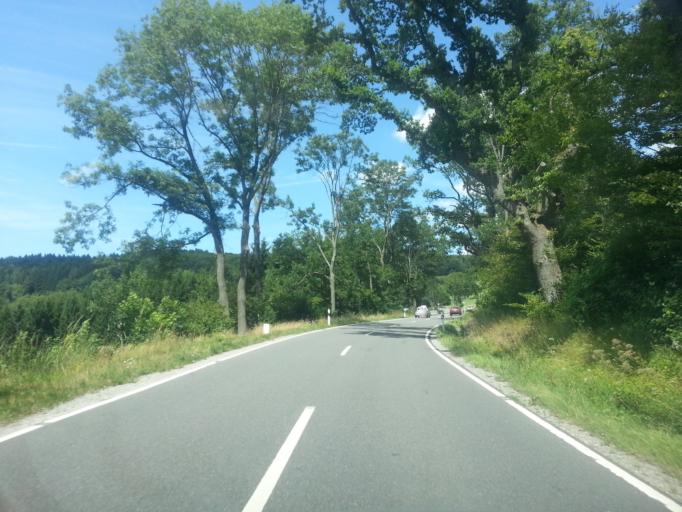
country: DE
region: Hesse
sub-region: Regierungsbezirk Darmstadt
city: Lindenfels
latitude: 49.6983
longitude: 8.7690
